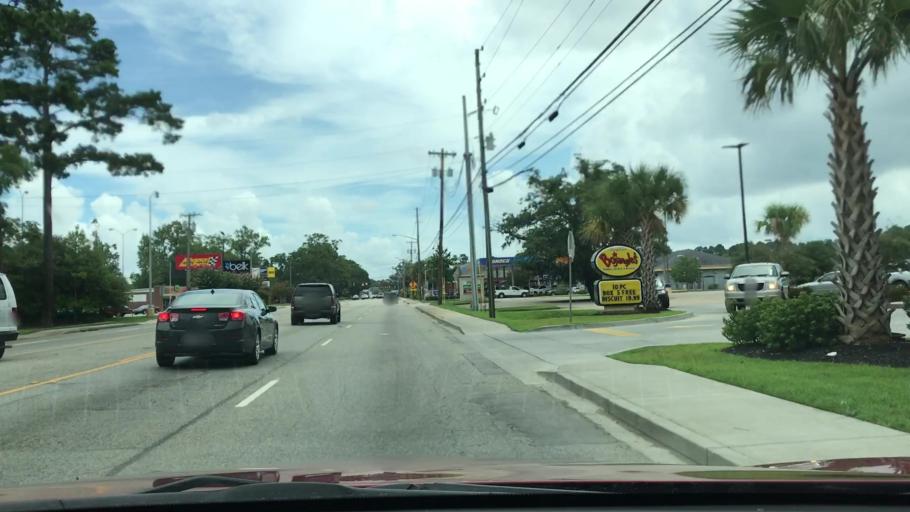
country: US
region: South Carolina
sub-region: Georgetown County
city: Georgetown
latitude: 33.3927
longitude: -79.2892
